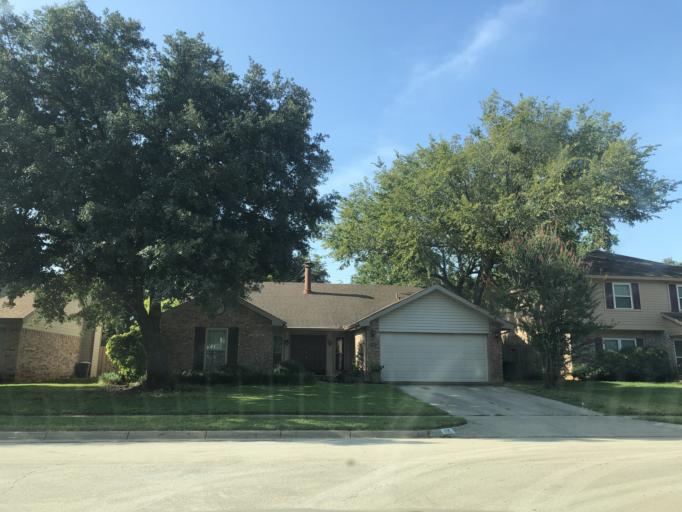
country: US
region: Texas
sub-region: Tarrant County
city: Euless
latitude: 32.8741
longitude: -97.0836
